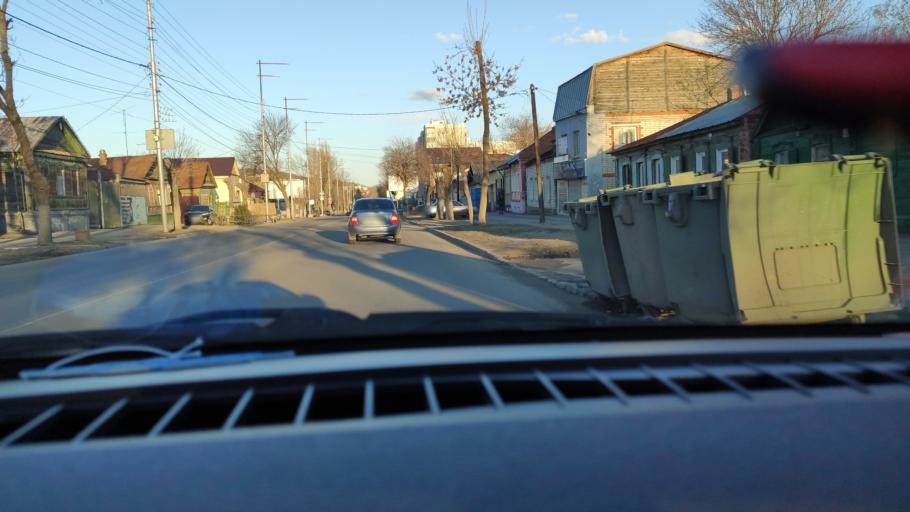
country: RU
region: Saratov
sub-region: Saratovskiy Rayon
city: Saratov
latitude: 51.5454
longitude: 46.0278
